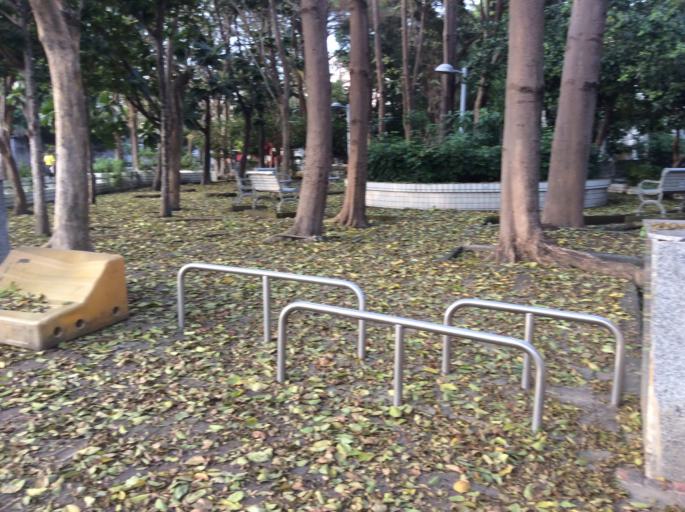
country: TW
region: Kaohsiung
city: Kaohsiung
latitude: 22.6938
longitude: 120.2891
